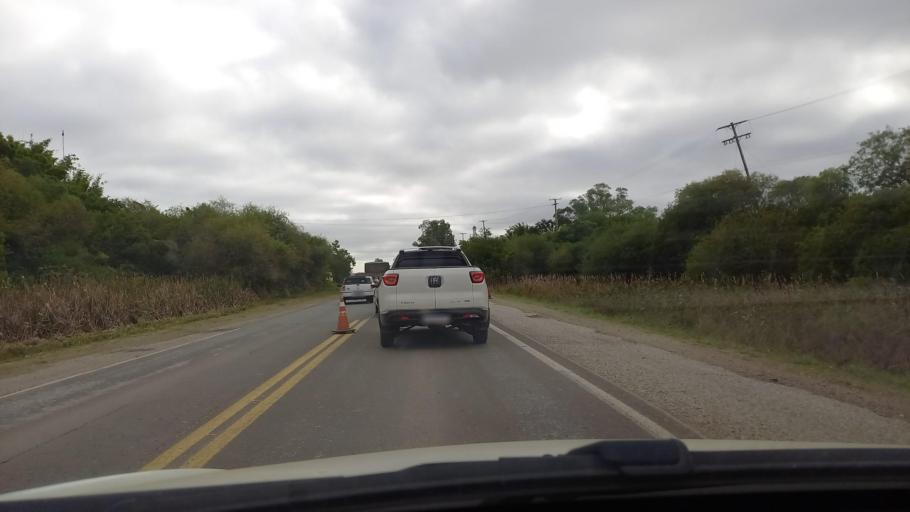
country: BR
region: Rio Grande do Sul
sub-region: Dom Pedrito
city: Dom Pedrito
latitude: -30.9600
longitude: -54.6786
